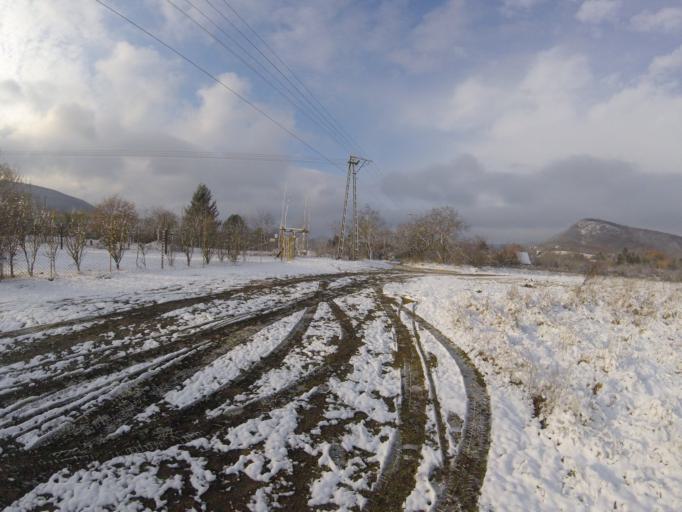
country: HU
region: Komarom-Esztergom
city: Esztergom
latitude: 47.7956
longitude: 18.8018
